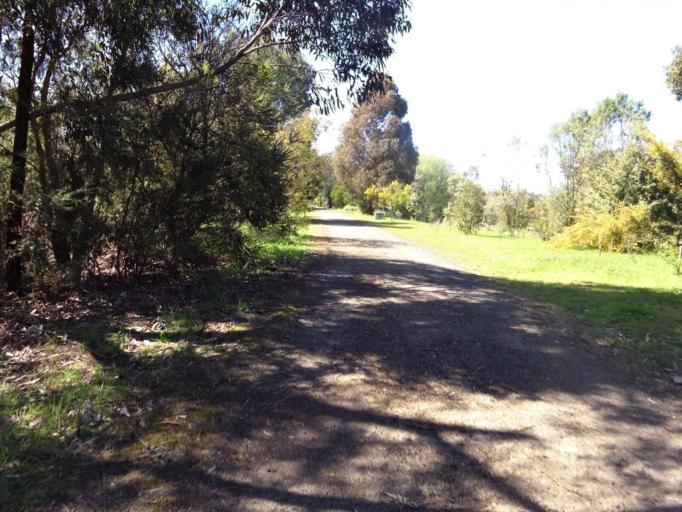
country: AU
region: Victoria
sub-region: Latrobe
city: Moe
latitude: -38.1771
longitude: 146.2683
